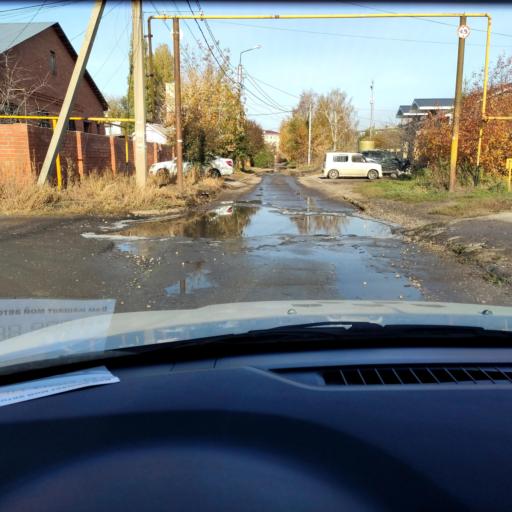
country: RU
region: Samara
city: Tol'yatti
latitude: 53.5297
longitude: 49.4242
